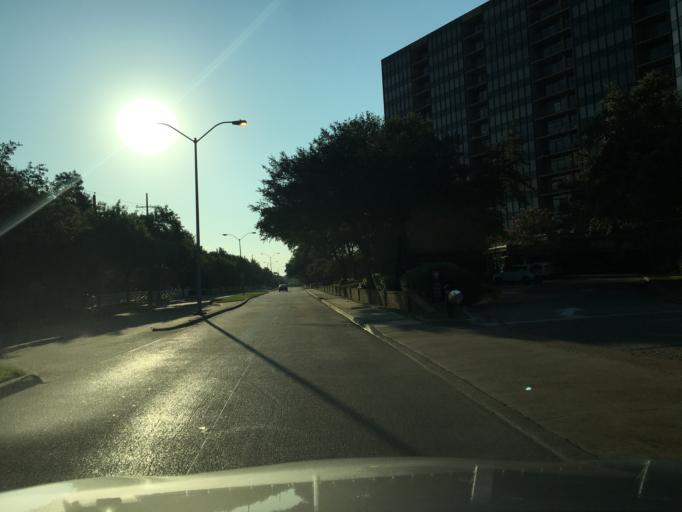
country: US
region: Texas
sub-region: Dallas County
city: Addison
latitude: 32.9685
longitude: -96.8193
